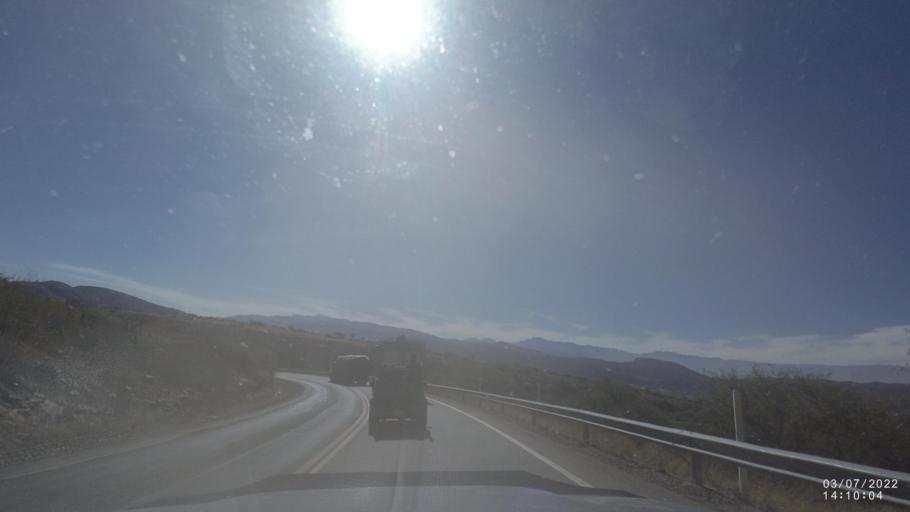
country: BO
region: Cochabamba
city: Capinota
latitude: -17.5991
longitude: -66.3598
